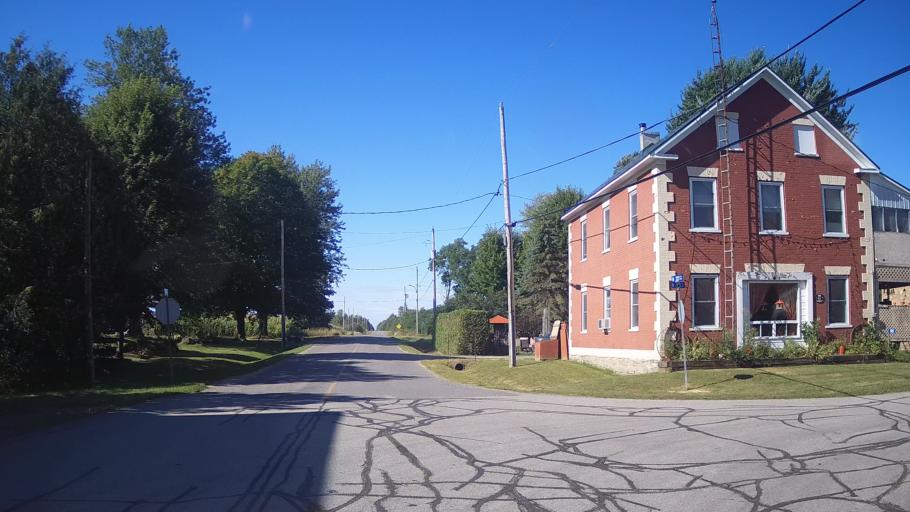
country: CA
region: Ontario
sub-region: Lanark County
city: Smiths Falls
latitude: 44.8375
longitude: -75.8856
